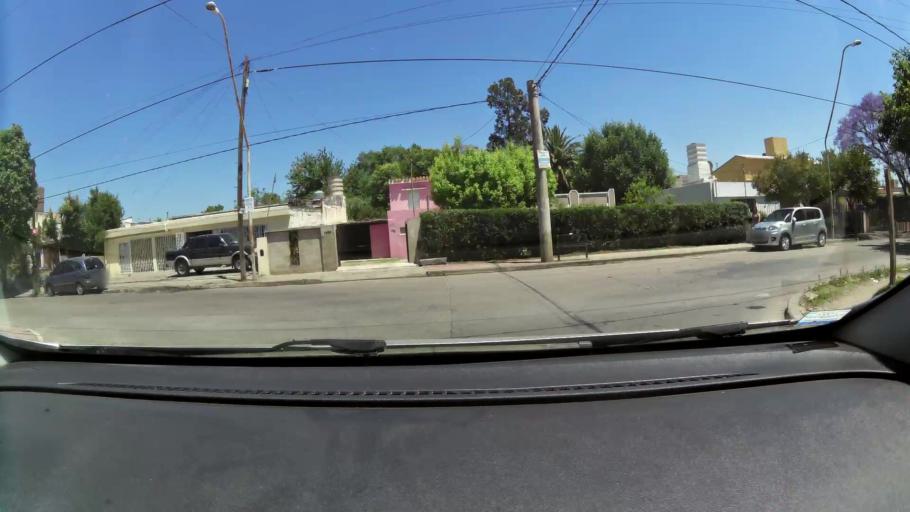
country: AR
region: Cordoba
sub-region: Departamento de Capital
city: Cordoba
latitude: -31.4179
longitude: -64.2323
